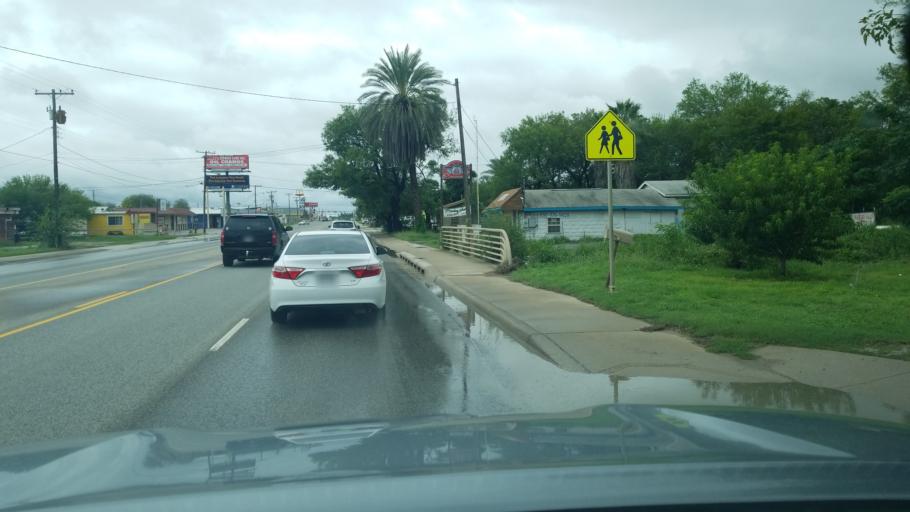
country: US
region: Texas
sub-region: Dimmit County
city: Carrizo Springs
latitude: 28.5266
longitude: -99.8550
